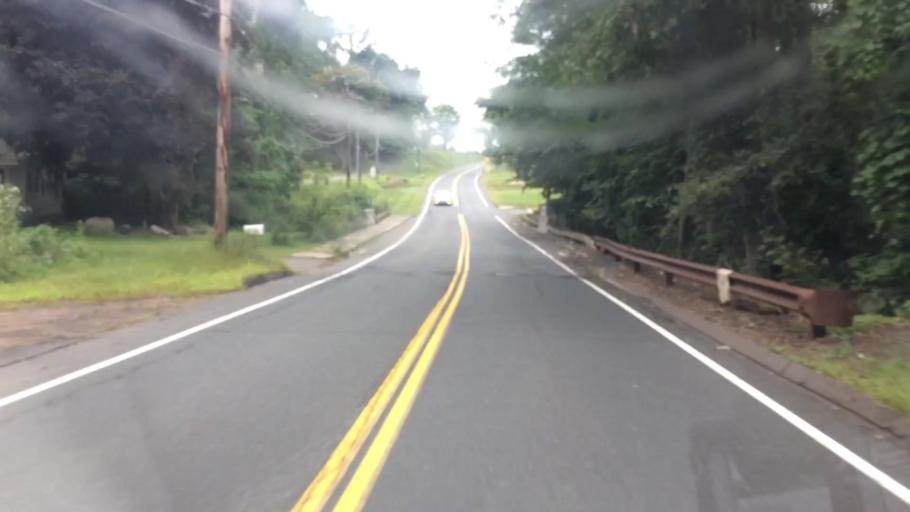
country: US
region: Connecticut
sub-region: Hartford County
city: Glastonbury Center
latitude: 41.6583
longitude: -72.6359
